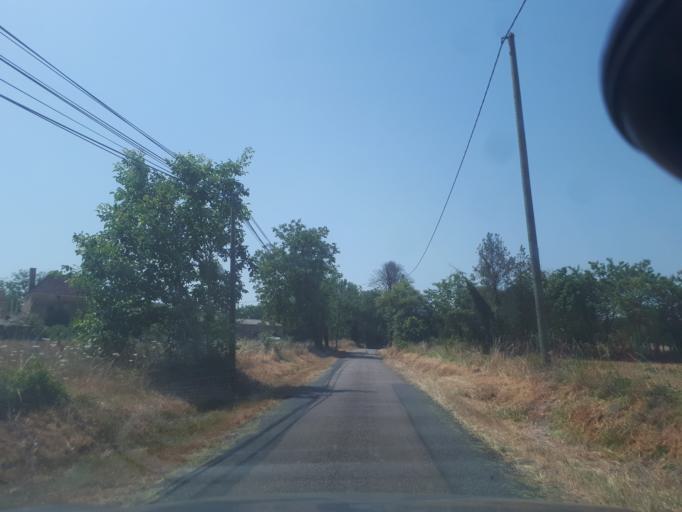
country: FR
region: Midi-Pyrenees
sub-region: Departement du Lot
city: Gourdon
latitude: 44.7747
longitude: 1.3639
